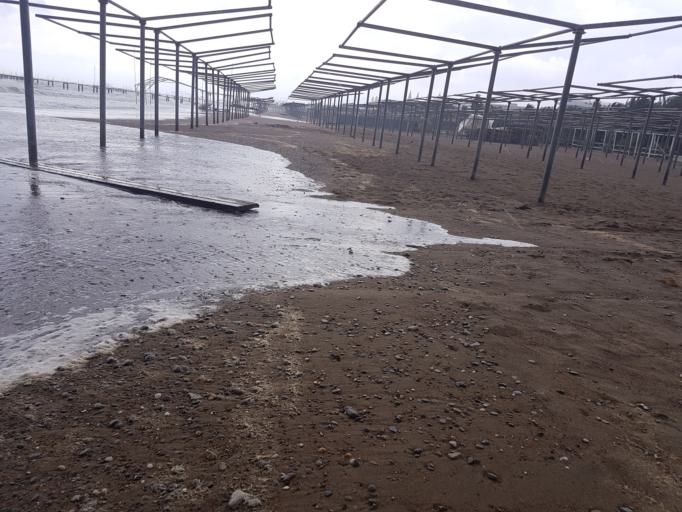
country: TR
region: Antalya
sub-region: Serik
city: Kumkoey
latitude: 36.8532
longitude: 30.8844
